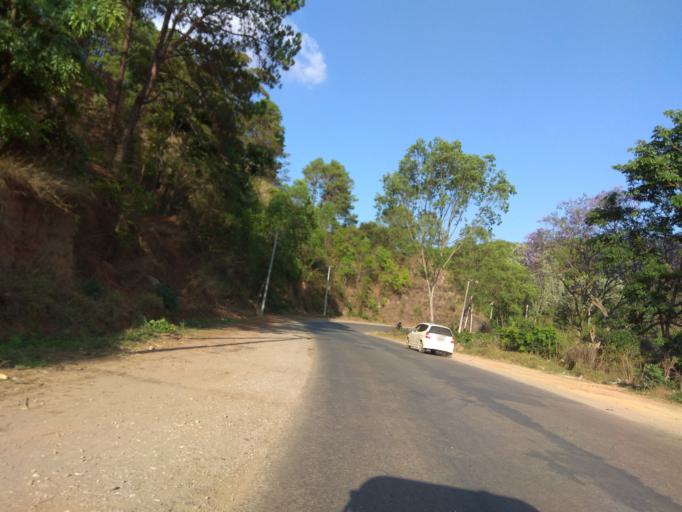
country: MM
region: Mandalay
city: Yamethin
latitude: 20.6323
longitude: 96.5792
